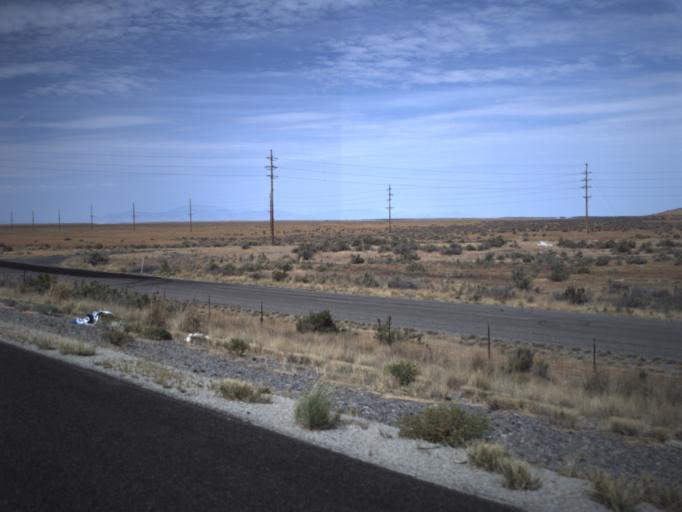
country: US
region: Utah
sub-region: Tooele County
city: Grantsville
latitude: 40.7261
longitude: -113.1411
